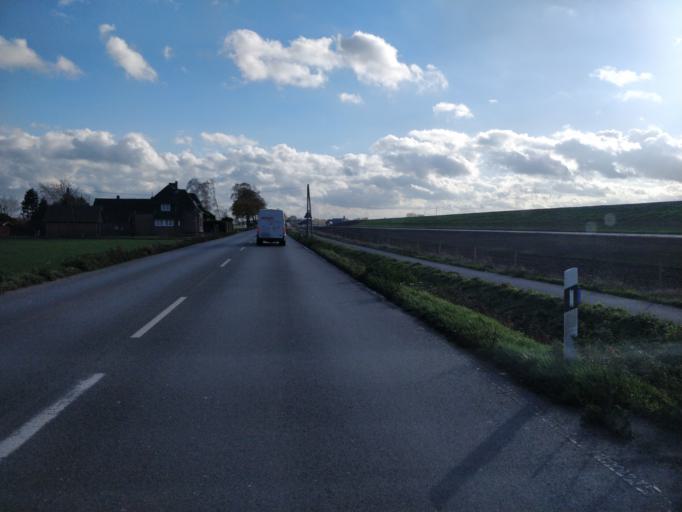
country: DE
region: North Rhine-Westphalia
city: Rees
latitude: 51.8108
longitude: 6.3647
